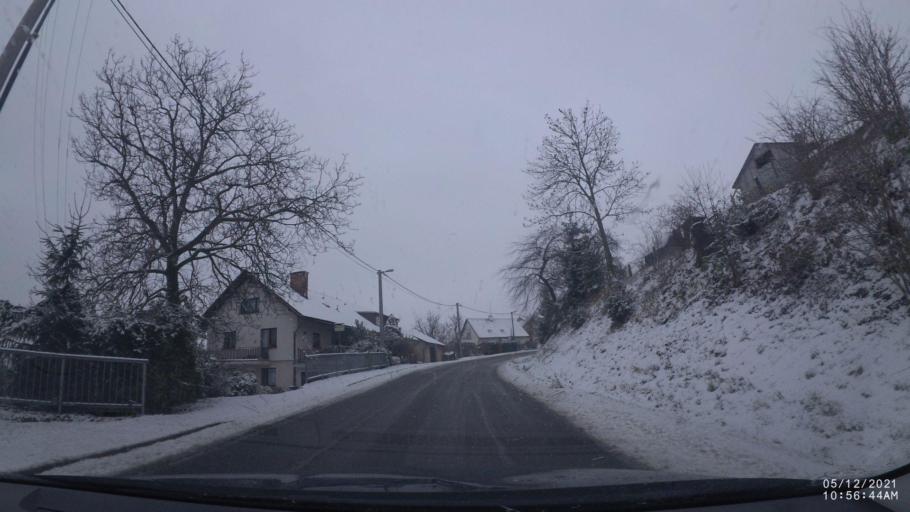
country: CZ
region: Kralovehradecky
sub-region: Okres Rychnov nad Kneznou
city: Rychnov nad Kneznou
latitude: 50.1655
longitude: 16.2675
